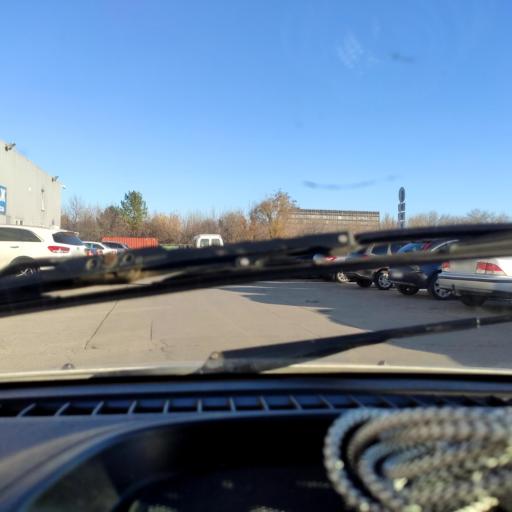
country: RU
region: Samara
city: Tol'yatti
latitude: 53.5486
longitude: 49.2680
